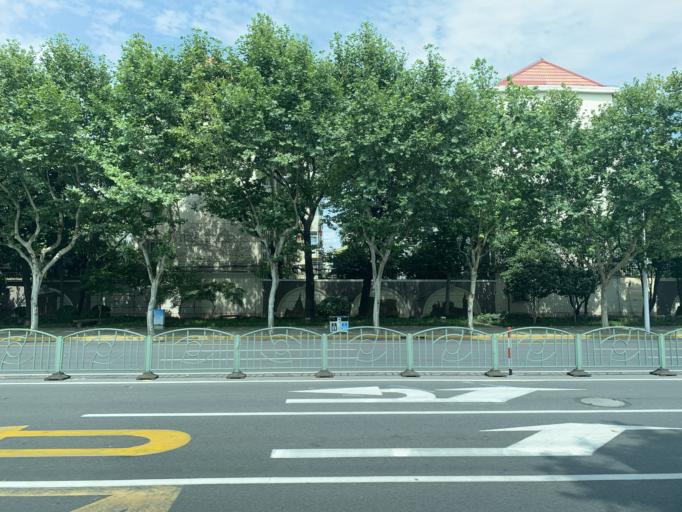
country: CN
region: Shanghai Shi
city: Pudong
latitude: 31.2355
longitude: 121.5187
